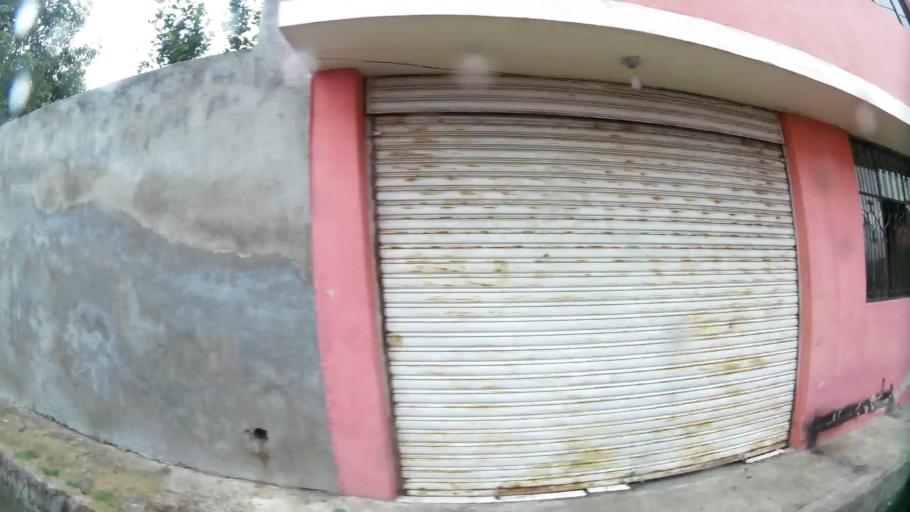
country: EC
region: Pichincha
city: Sangolqui
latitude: -0.2767
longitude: -78.4693
